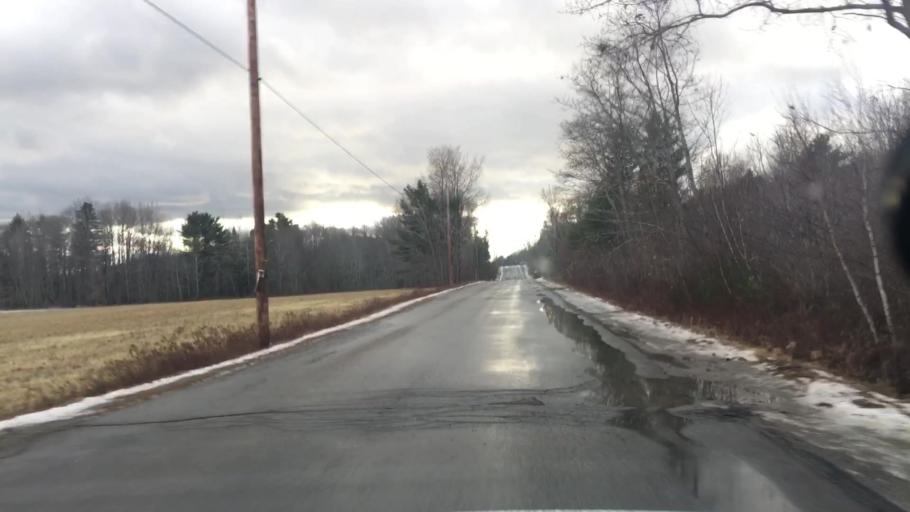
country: US
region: Maine
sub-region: Hancock County
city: Dedham
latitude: 44.6356
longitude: -68.7058
